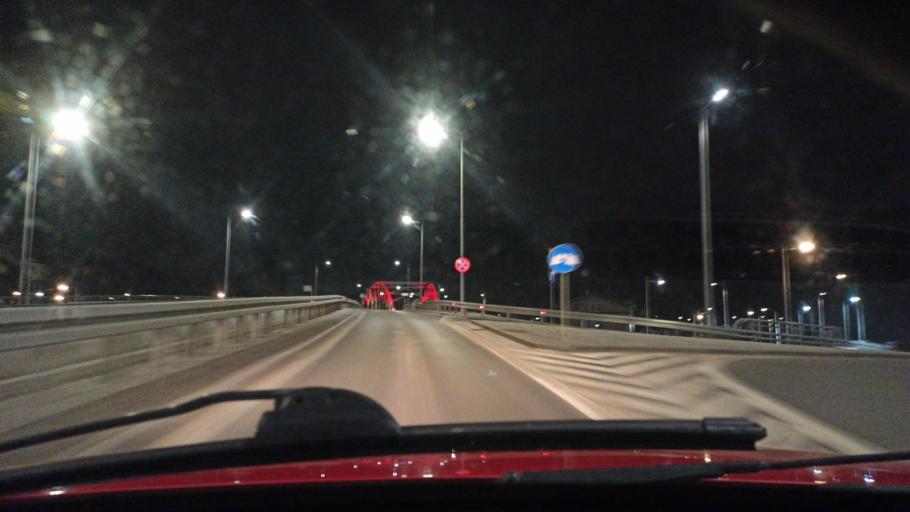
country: PL
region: Warmian-Masurian Voivodeship
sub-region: Powiat elblaski
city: Elblag
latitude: 54.1528
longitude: 19.4122
